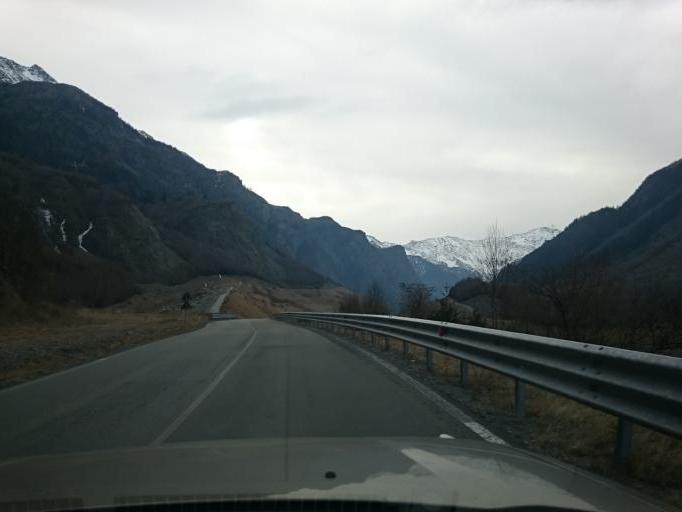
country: IT
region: Lombardy
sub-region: Provincia di Sondrio
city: Valdisotto
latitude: 46.3911
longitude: 10.3537
